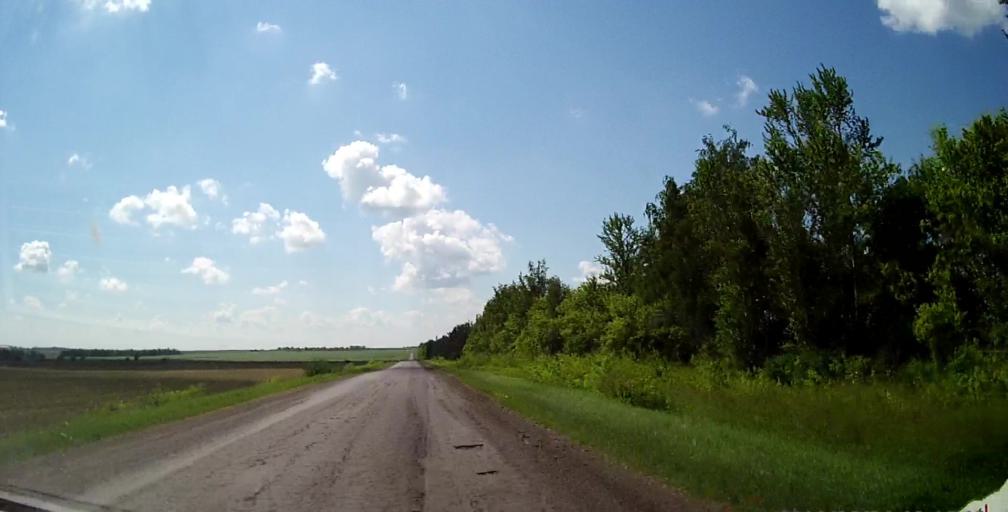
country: RU
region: Lipetsk
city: Chaplygin
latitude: 53.2888
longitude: 39.9586
